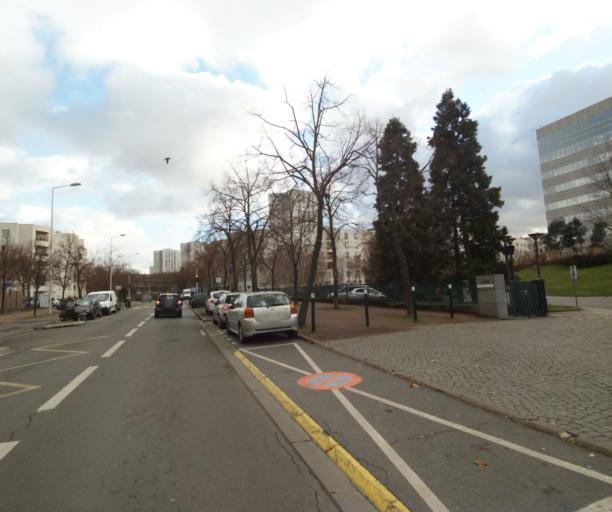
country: FR
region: Ile-de-France
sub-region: Departement des Hauts-de-Seine
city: Nanterre
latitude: 48.8913
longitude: 2.2152
